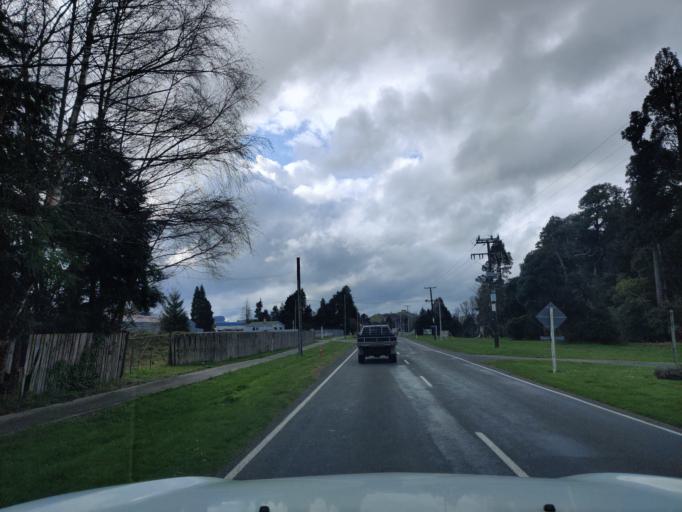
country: NZ
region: Manawatu-Wanganui
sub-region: Ruapehu District
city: Waiouru
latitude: -39.4333
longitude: 175.2830
